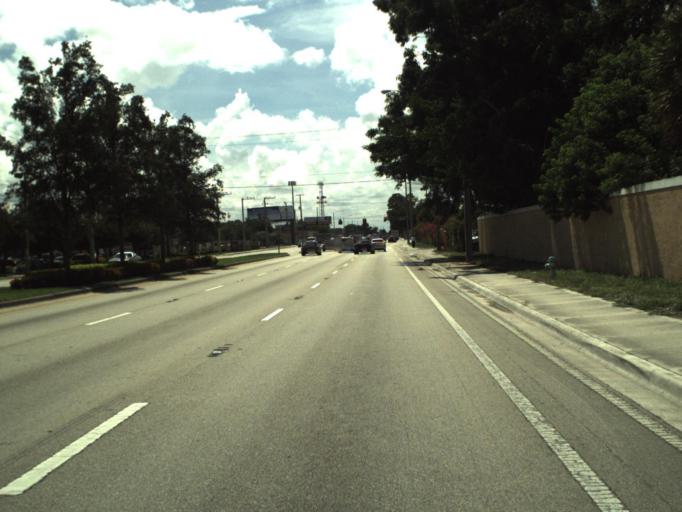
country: US
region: Florida
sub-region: Broward County
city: Pembroke Park
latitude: 25.9957
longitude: -80.1807
